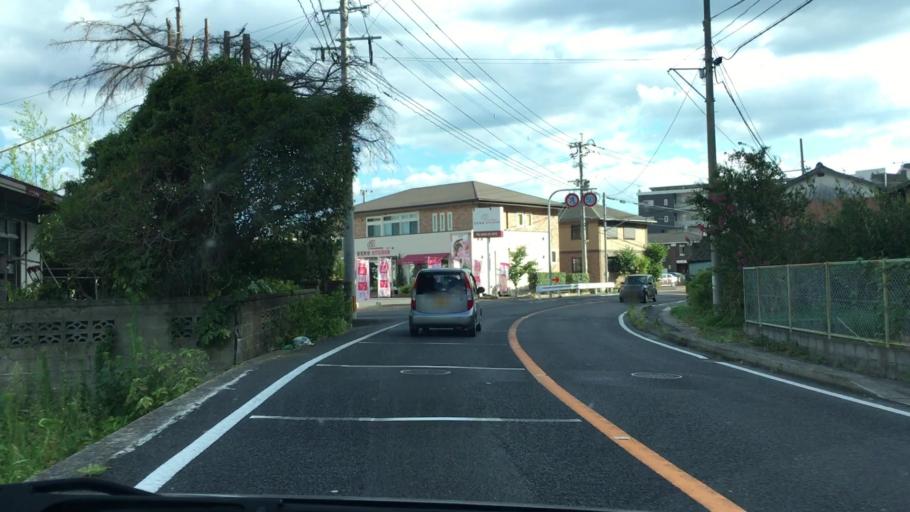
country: JP
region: Nagasaki
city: Sasebo
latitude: 33.1337
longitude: 129.7953
